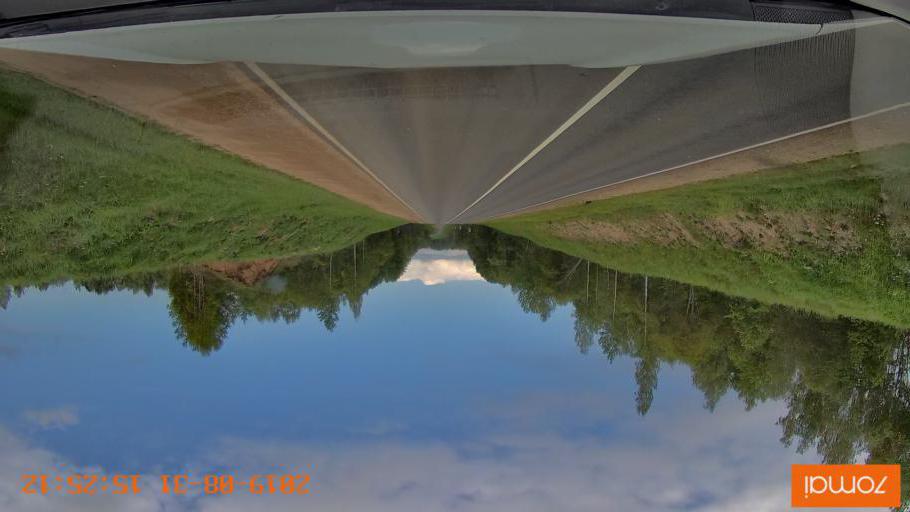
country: RU
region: Kaluga
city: Baryatino
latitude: 54.5381
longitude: 34.5161
